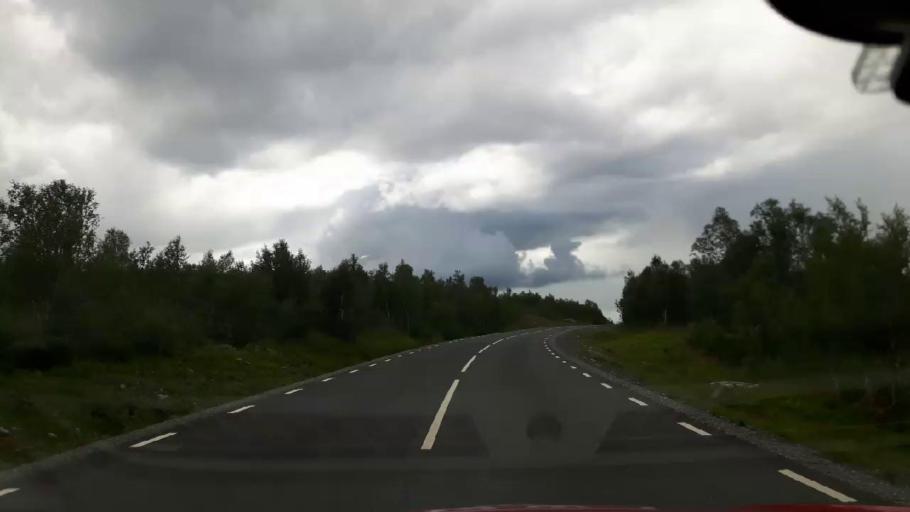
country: NO
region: Nord-Trondelag
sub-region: Royrvik
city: Royrvik
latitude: 64.9741
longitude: 14.2127
